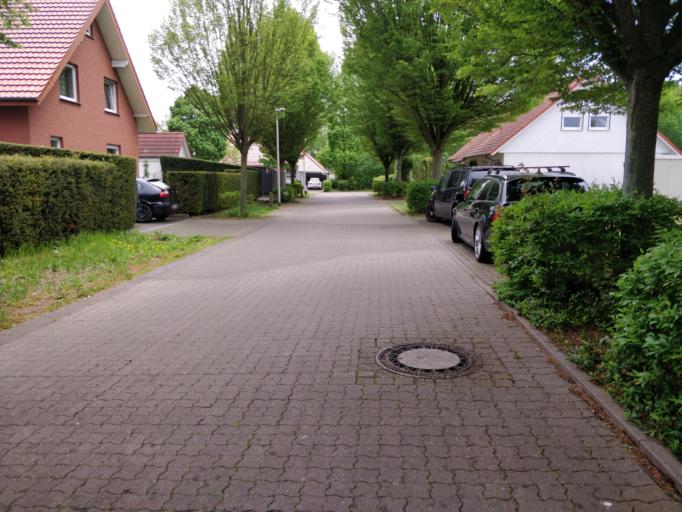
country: DE
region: North Rhine-Westphalia
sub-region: Regierungsbezirk Detmold
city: Minden
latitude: 52.2986
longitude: 8.8669
